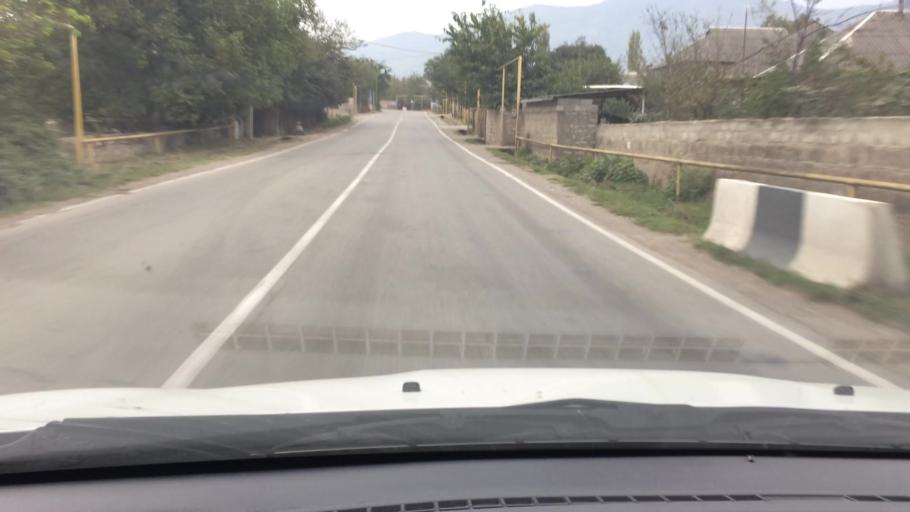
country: AM
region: Tavush
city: Bagratashen
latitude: 41.2393
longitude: 44.8019
